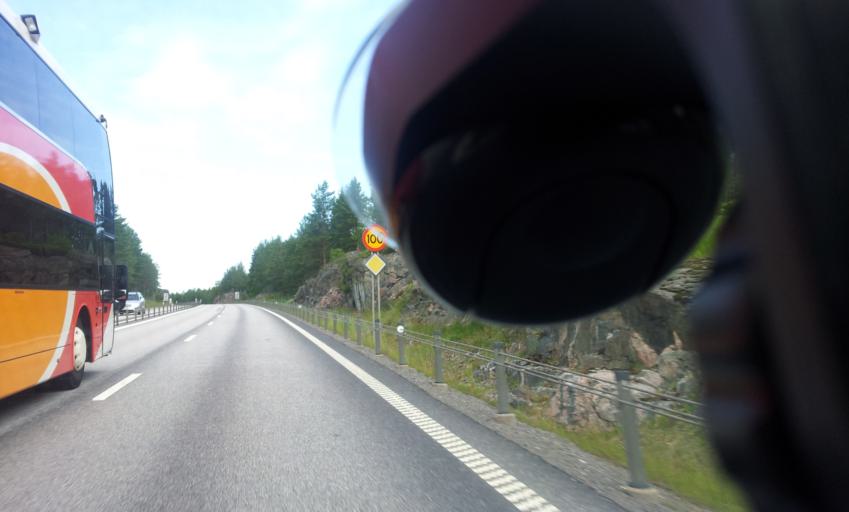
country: SE
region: OEstergoetland
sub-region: Valdemarsviks Kommun
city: Valdemarsvik
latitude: 58.2312
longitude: 16.5517
